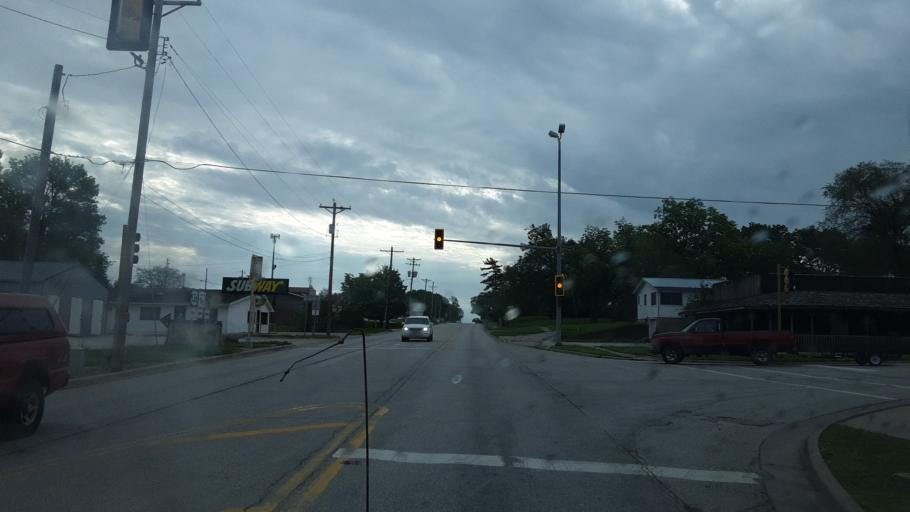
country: US
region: Illinois
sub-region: Hancock County
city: Hamilton
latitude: 40.3965
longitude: -91.3400
